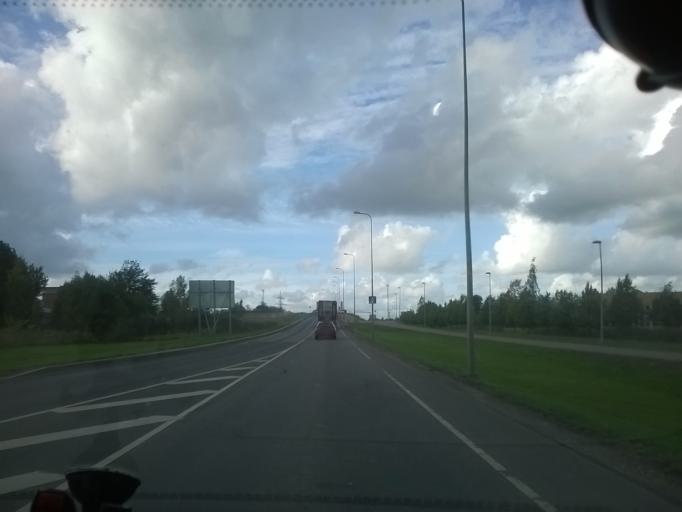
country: EE
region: Harju
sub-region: Tallinna linn
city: Kose
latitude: 59.4182
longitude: 24.8438
